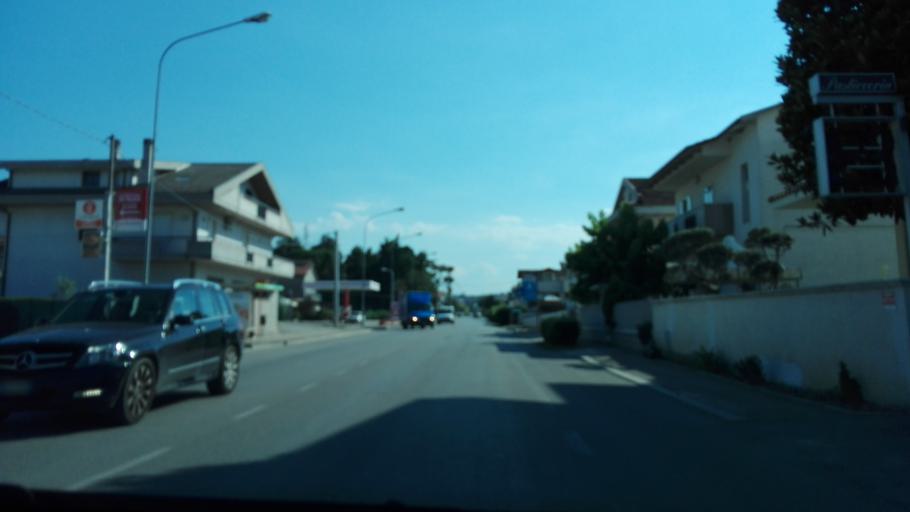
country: IT
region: Abruzzo
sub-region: Provincia di Pescara
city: Cappelle sul Tavo
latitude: 42.4889
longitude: 14.1212
